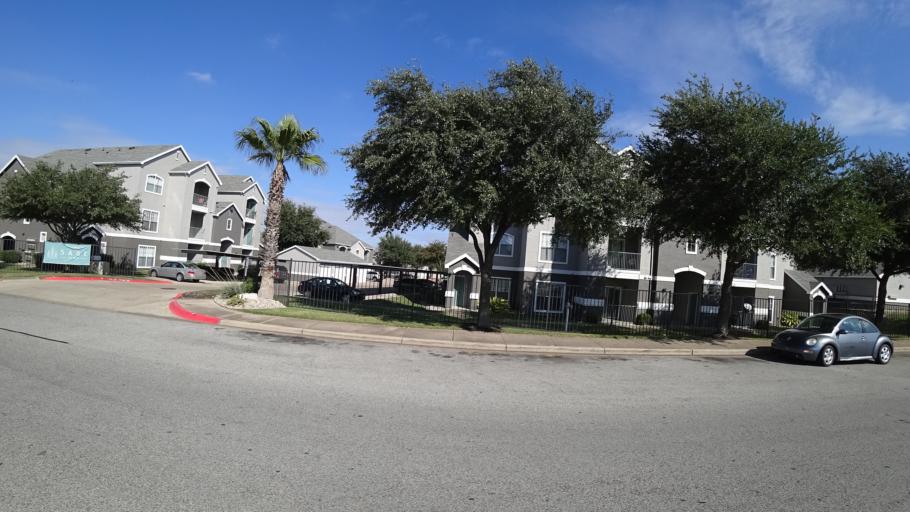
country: US
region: Texas
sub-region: Travis County
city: Windemere
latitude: 30.4499
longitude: -97.6529
